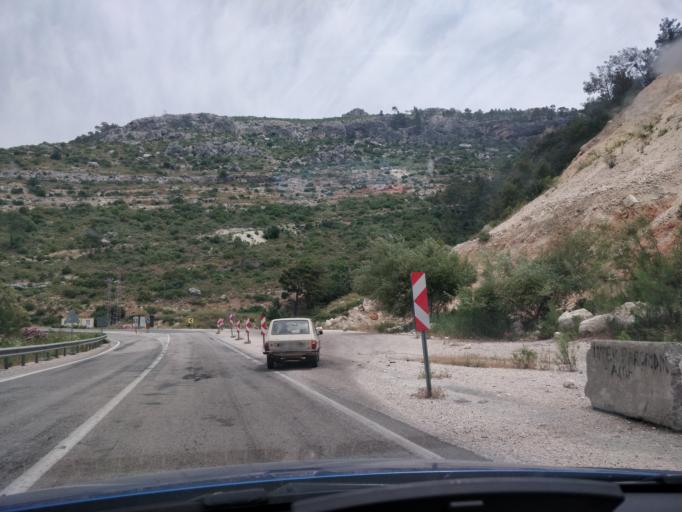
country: TR
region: Mersin
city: Tasucu
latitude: 36.3921
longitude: 33.8387
